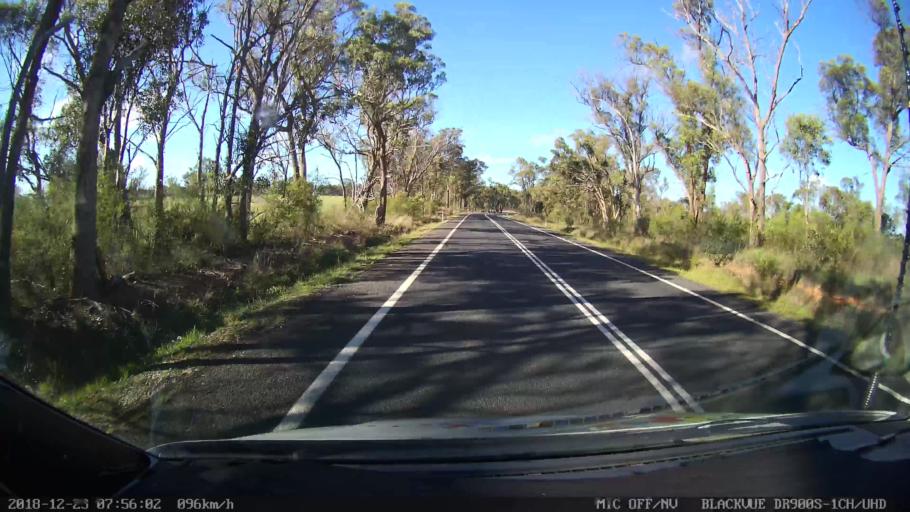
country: AU
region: New South Wales
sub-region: Armidale Dumaresq
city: Armidale
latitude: -30.5442
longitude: 151.7717
